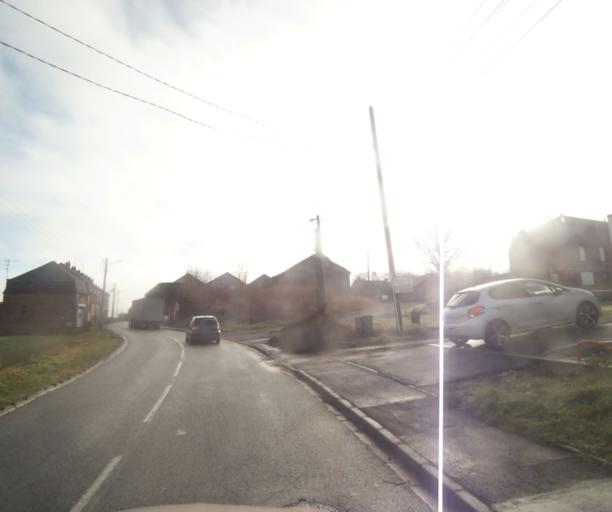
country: FR
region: Nord-Pas-de-Calais
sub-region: Departement du Nord
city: Artres
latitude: 50.2860
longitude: 3.5470
